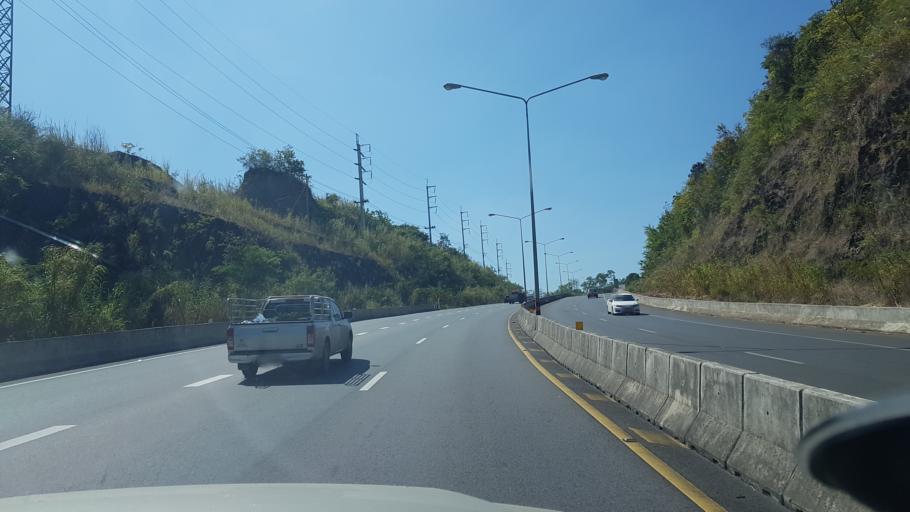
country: TH
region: Phetchabun
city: Khao Kho
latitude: 16.7723
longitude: 101.0592
